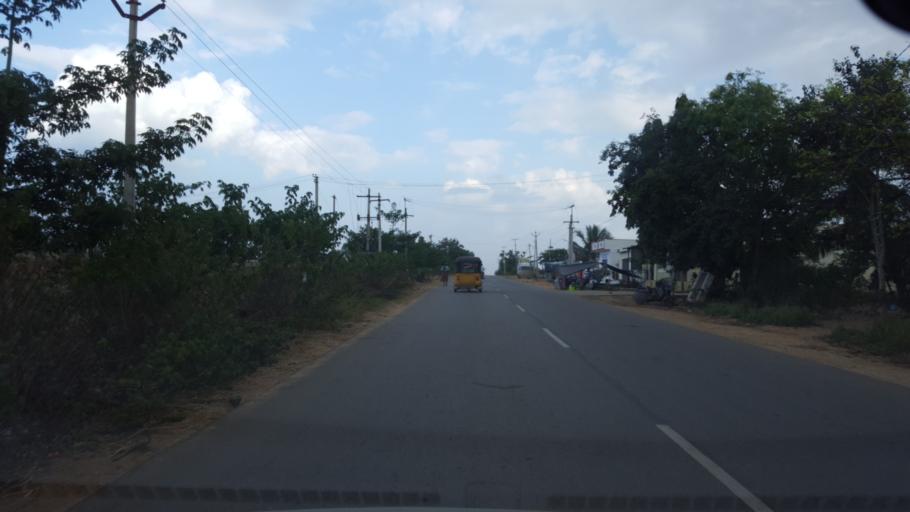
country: IN
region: Telangana
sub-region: Mahbubnagar
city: Mahbubnagar
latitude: 16.7601
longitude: 77.9568
